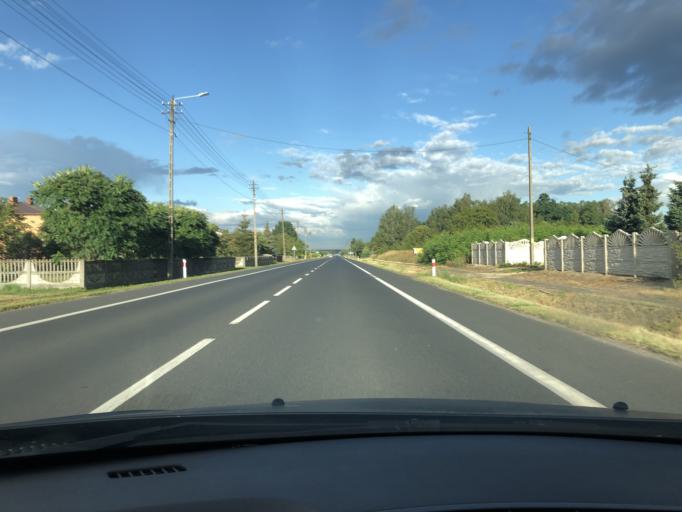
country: PL
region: Lodz Voivodeship
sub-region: Powiat wieruszowski
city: Galewice
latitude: 51.3033
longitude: 18.2816
